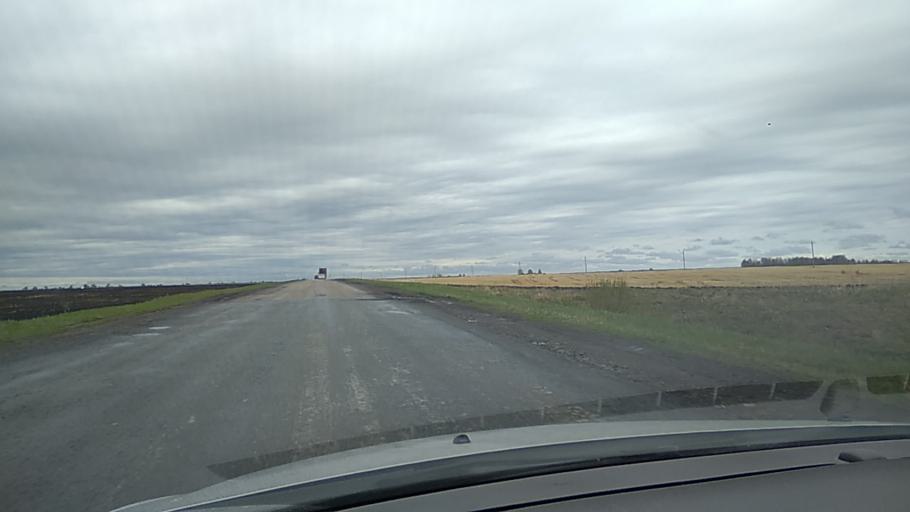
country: RU
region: Kurgan
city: Shatrovo
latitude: 56.4051
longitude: 64.9491
